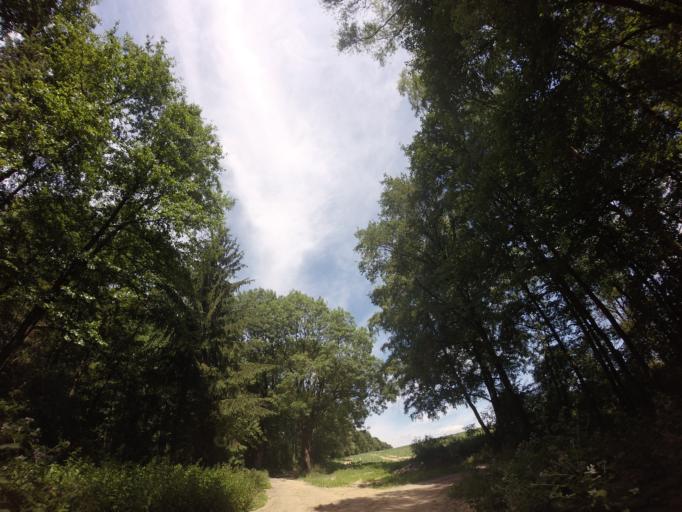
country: PL
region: West Pomeranian Voivodeship
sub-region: Powiat choszczenski
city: Recz
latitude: 53.2702
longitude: 15.5317
